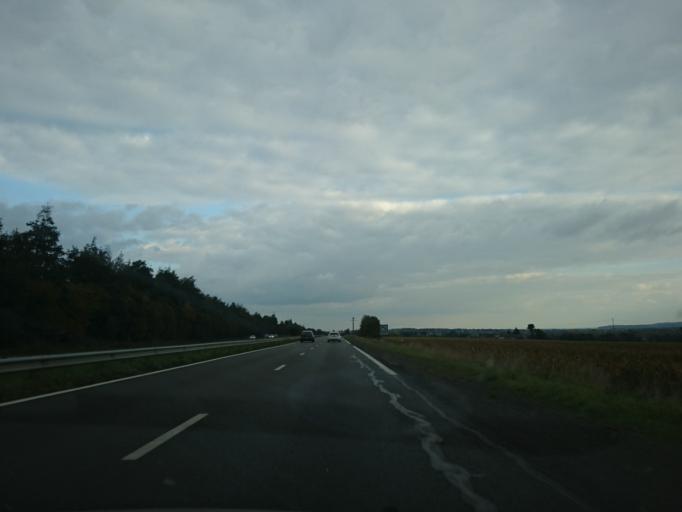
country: FR
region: Brittany
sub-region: Departement d'Ille-et-Vilaine
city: Montauban-de-Bretagne
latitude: 48.1899
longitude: -2.0177
